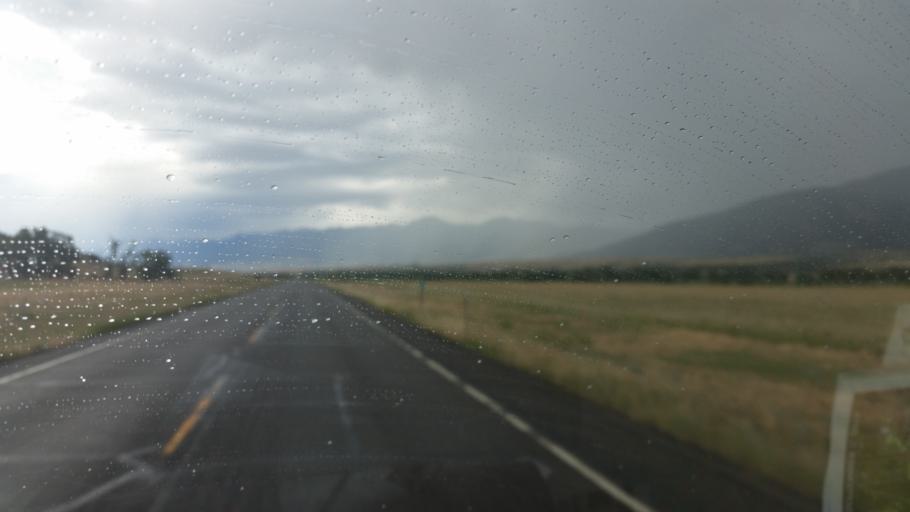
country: US
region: Montana
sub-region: Park County
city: Livingston
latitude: 45.3253
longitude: -110.7876
